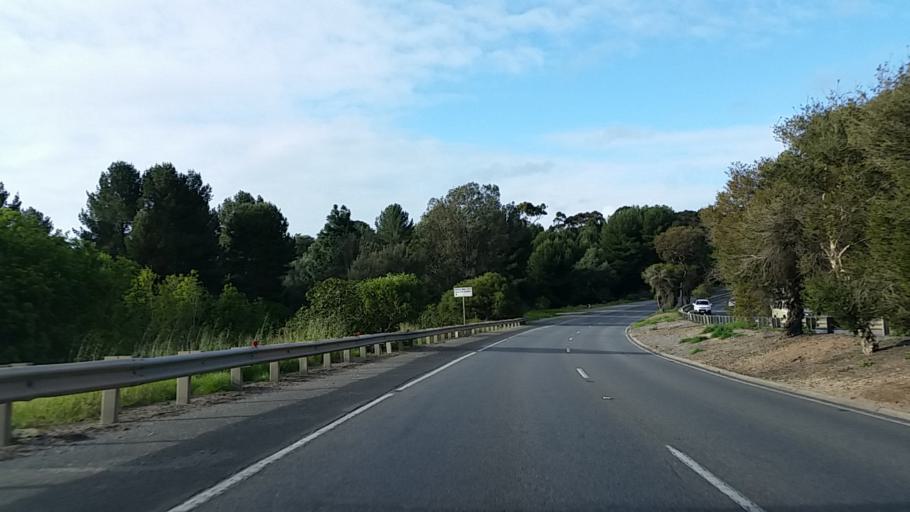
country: AU
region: South Australia
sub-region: Marion
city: Happy Valley
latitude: -35.0895
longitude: 138.5377
